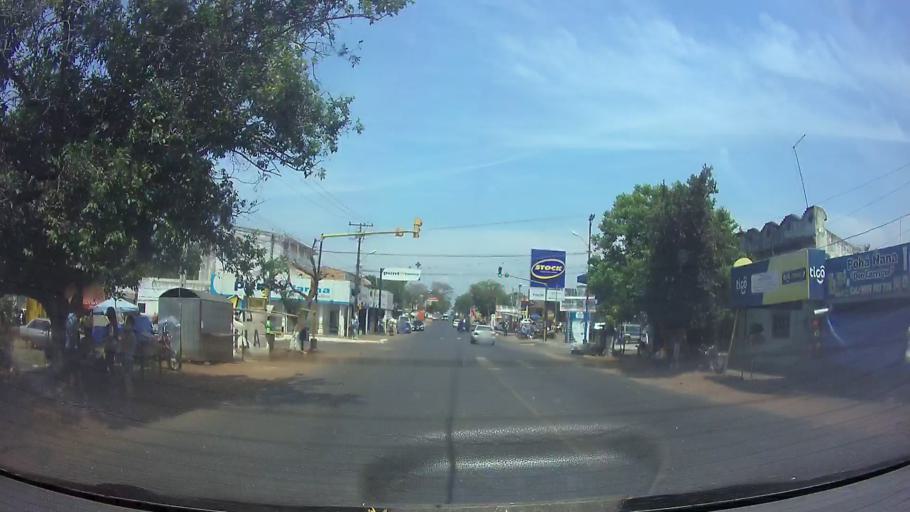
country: PY
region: Central
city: Guarambare
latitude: -25.4410
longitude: -57.4428
